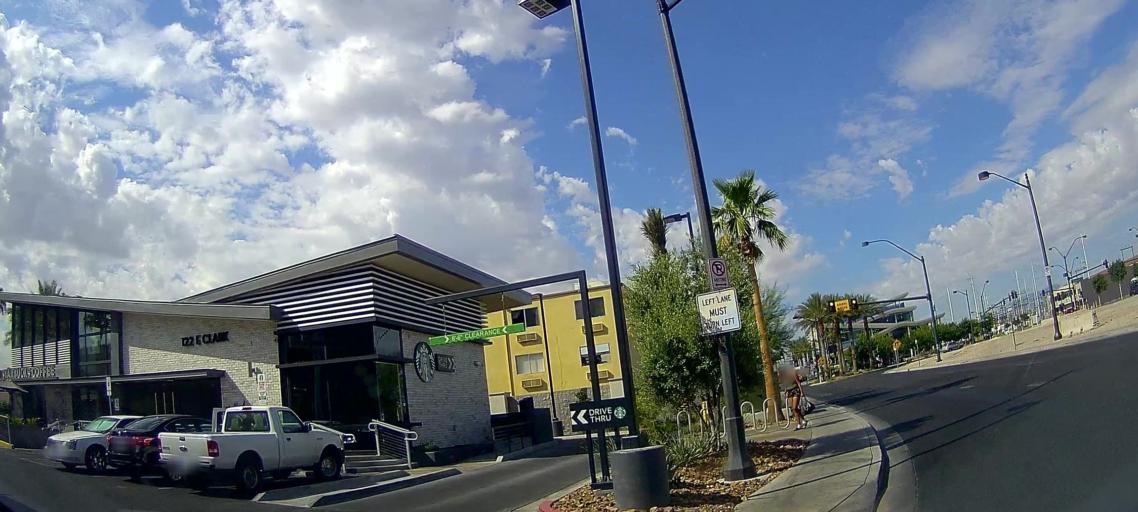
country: US
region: Nevada
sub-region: Clark County
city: Las Vegas
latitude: 36.1660
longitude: -115.1479
